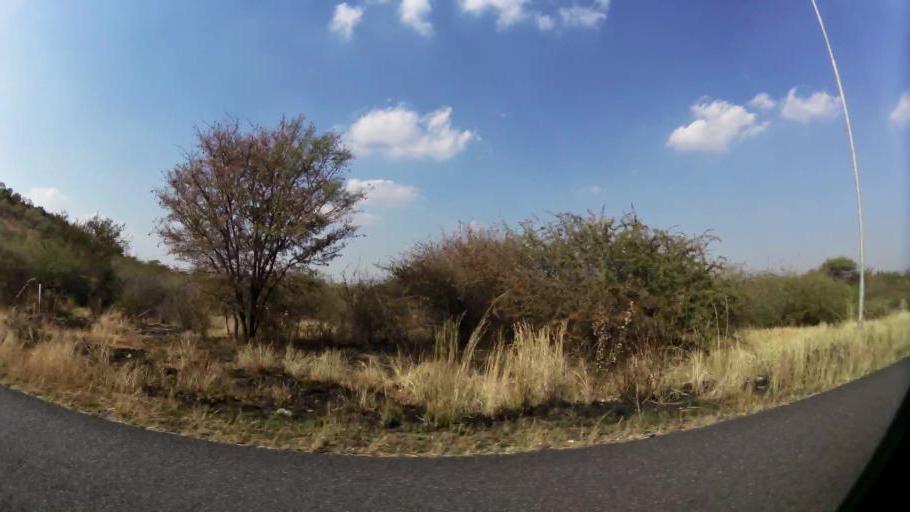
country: ZA
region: North-West
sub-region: Bojanala Platinum District Municipality
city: Rustenburg
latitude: -25.5723
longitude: 27.1399
